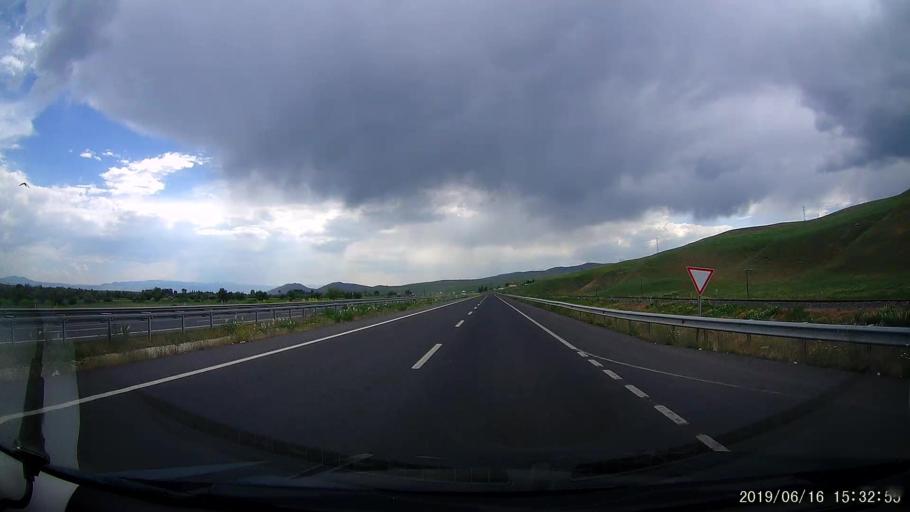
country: TR
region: Erzurum
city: Horasan
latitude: 40.0295
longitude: 42.0341
